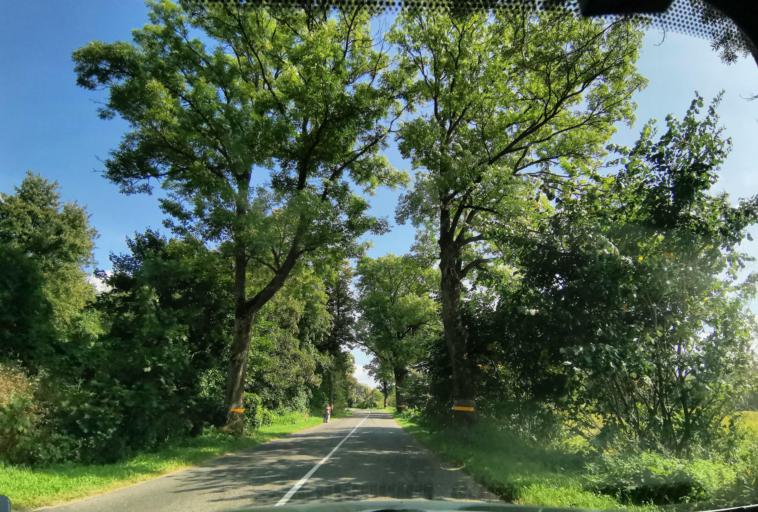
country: RU
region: Kaliningrad
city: Chernyakhovsk
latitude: 54.6487
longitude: 21.7719
